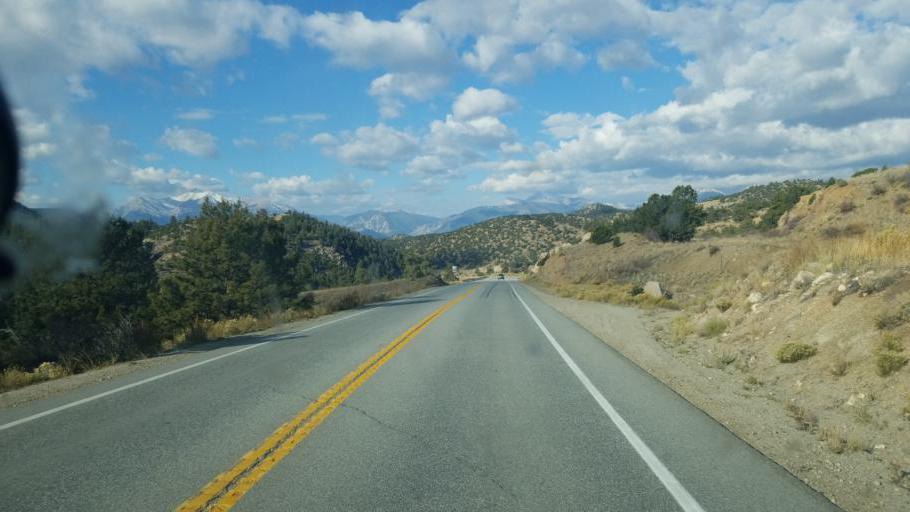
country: US
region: Colorado
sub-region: Chaffee County
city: Buena Vista
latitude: 38.8410
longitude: -106.0004
